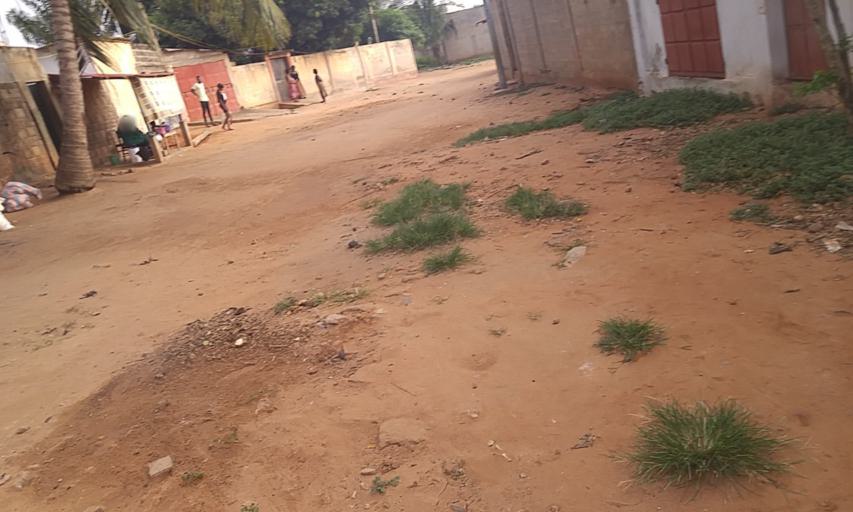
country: TG
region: Maritime
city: Lome
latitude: 6.1732
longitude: 1.1712
